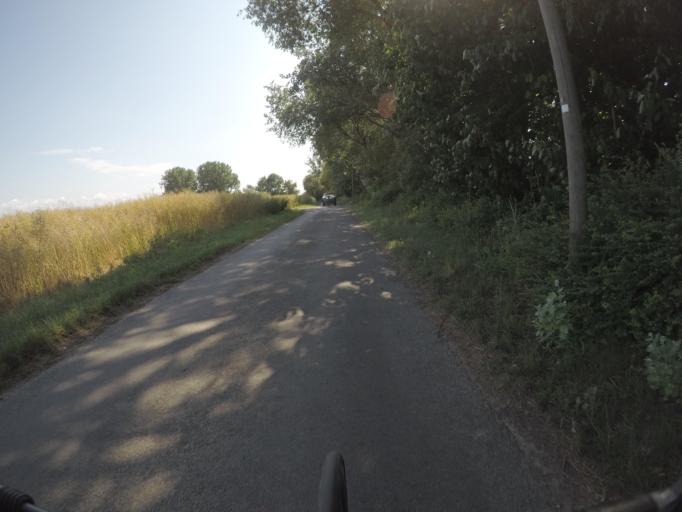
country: DE
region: Mecklenburg-Vorpommern
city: Rambin
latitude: 54.4322
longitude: 13.1710
